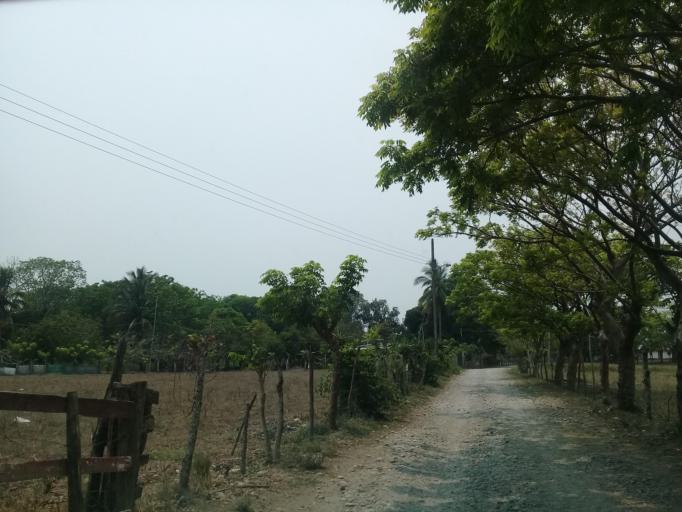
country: MX
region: Veracruz
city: Jamapa
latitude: 18.9319
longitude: -96.2117
